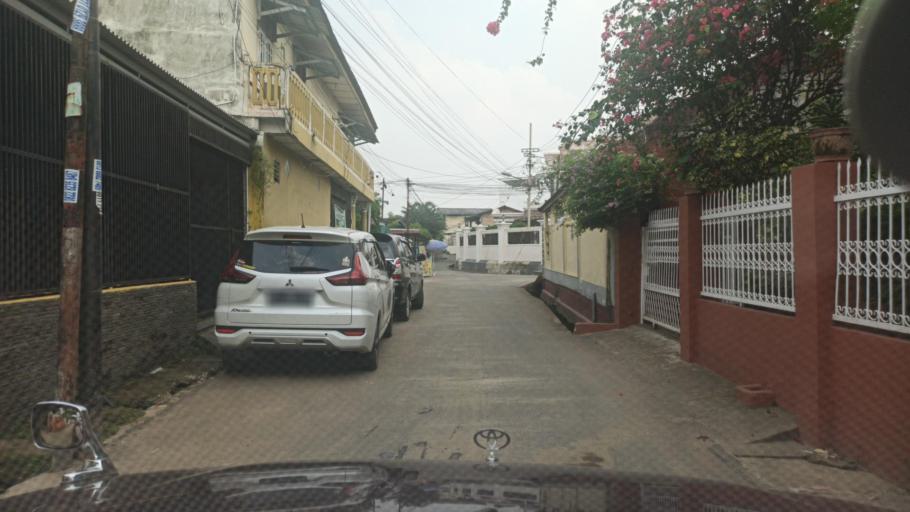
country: ID
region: South Sumatra
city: Plaju
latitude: -2.9914
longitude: 104.7398
